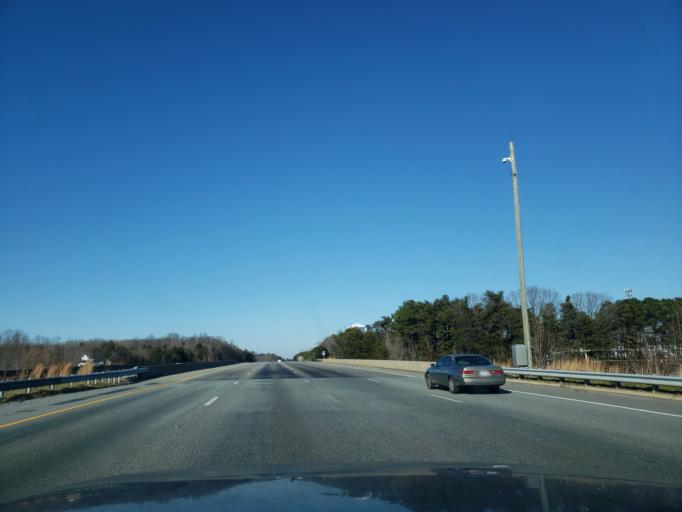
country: US
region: North Carolina
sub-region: Guilford County
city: High Point
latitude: 35.9658
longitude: -79.9746
